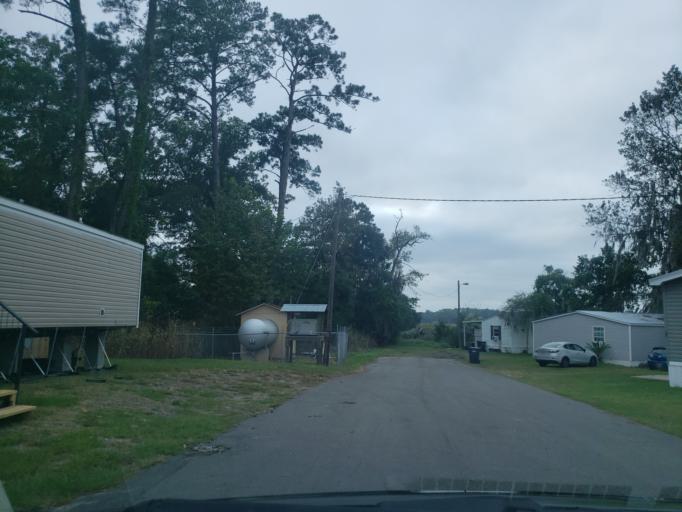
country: US
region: Georgia
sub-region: Chatham County
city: Montgomery
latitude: 31.9573
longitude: -81.1077
